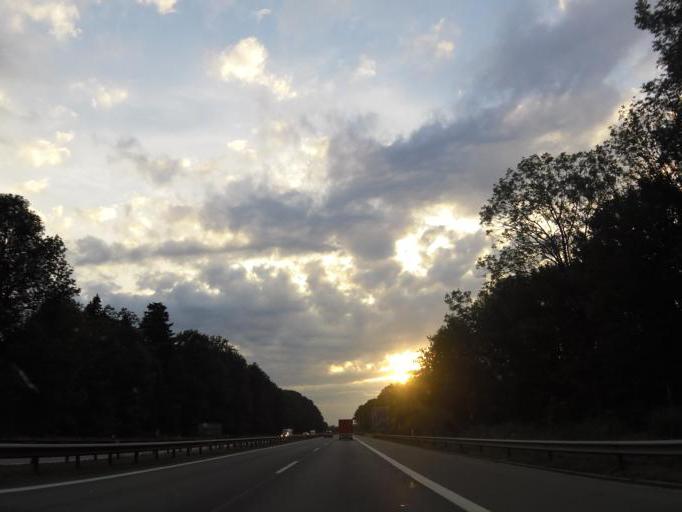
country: DE
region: Bavaria
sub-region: Upper Bavaria
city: Ubersee
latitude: 47.8356
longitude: 12.4994
